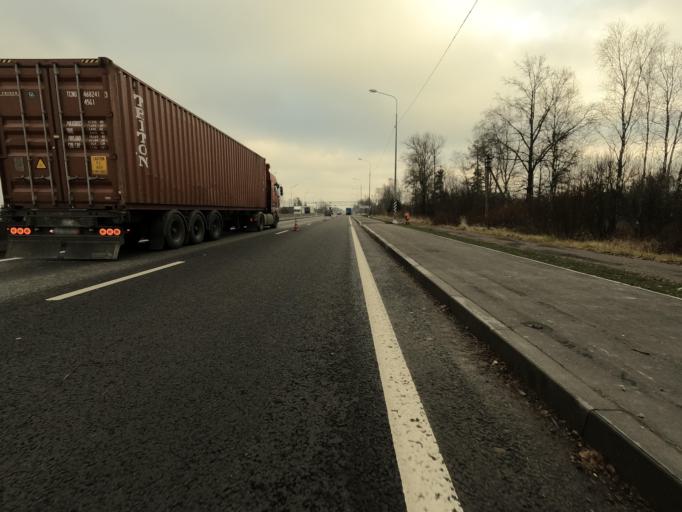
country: RU
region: Leningrad
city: Mga
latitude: 59.7210
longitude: 31.1011
